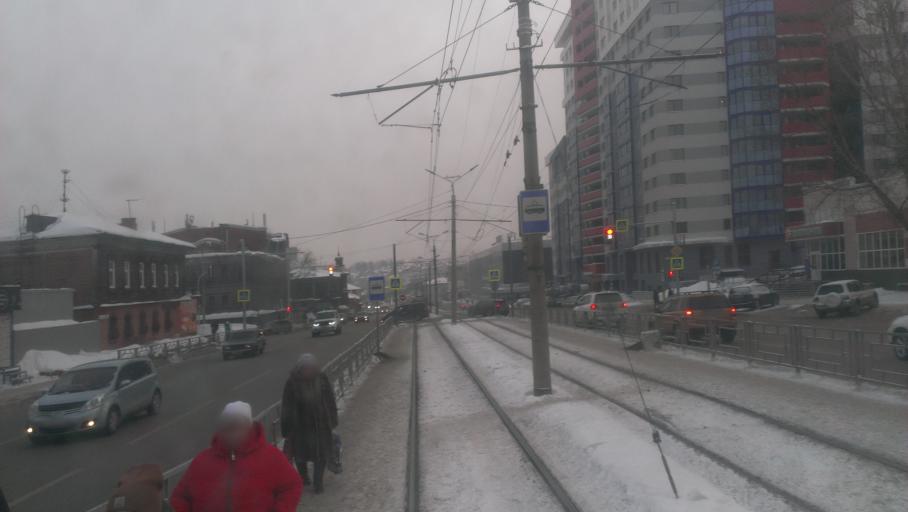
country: RU
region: Altai Krai
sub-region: Gorod Barnaulskiy
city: Barnaul
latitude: 53.3328
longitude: 83.7801
